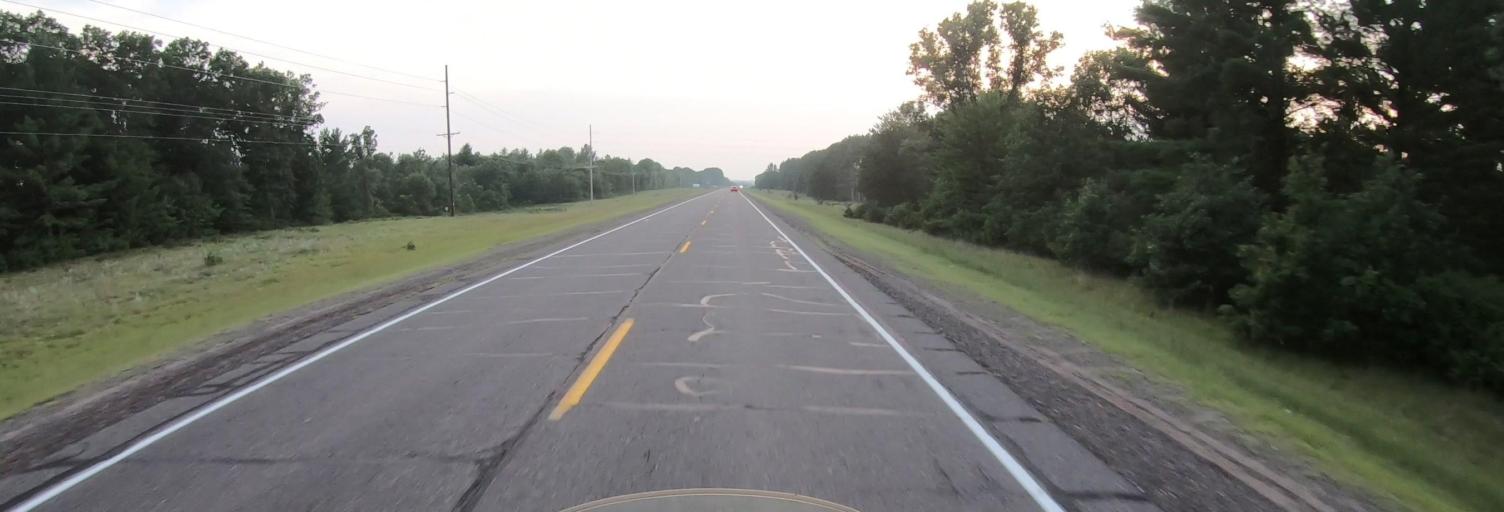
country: US
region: Wisconsin
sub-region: Burnett County
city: Grantsburg
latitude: 45.7730
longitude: -92.7532
